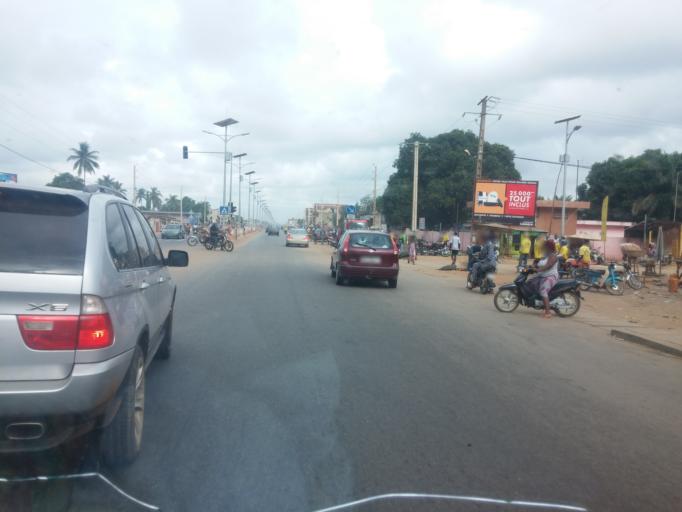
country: BJ
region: Atlantique
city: Hevie
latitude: 6.3880
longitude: 2.2723
